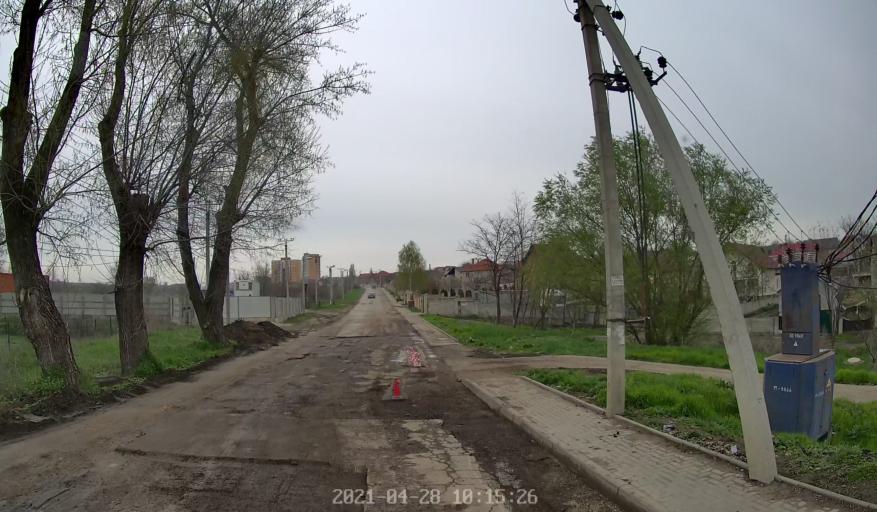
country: MD
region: Chisinau
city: Chisinau
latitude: 46.9883
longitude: 28.9331
